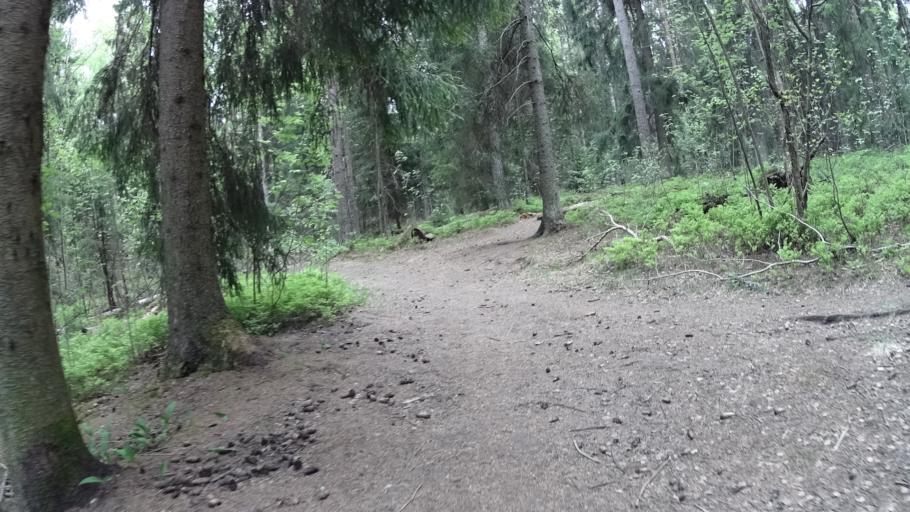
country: FI
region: Uusimaa
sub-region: Helsinki
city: Kilo
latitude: 60.2537
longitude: 24.7951
